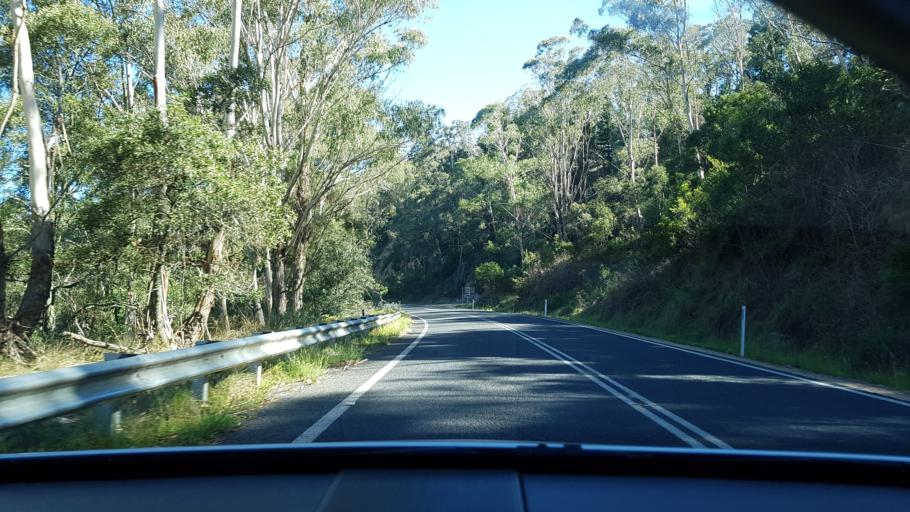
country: AU
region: New South Wales
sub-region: Lithgow
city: Bowenfels
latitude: -33.6645
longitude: 150.0502
